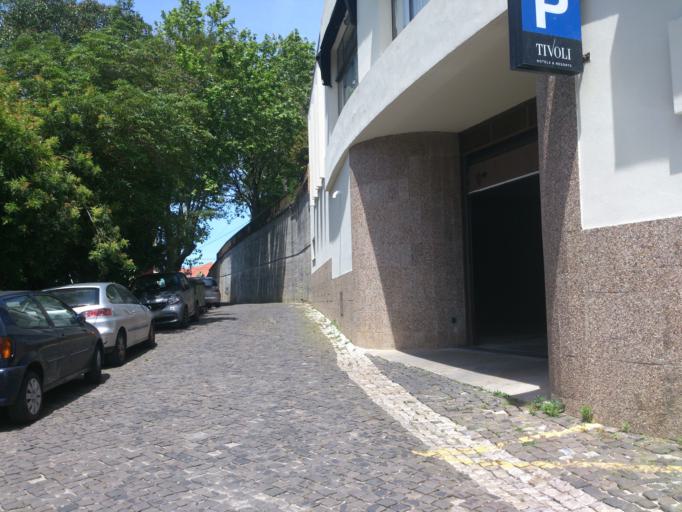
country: PT
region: Lisbon
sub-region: Sintra
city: Sintra
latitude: 38.7976
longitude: -9.3919
